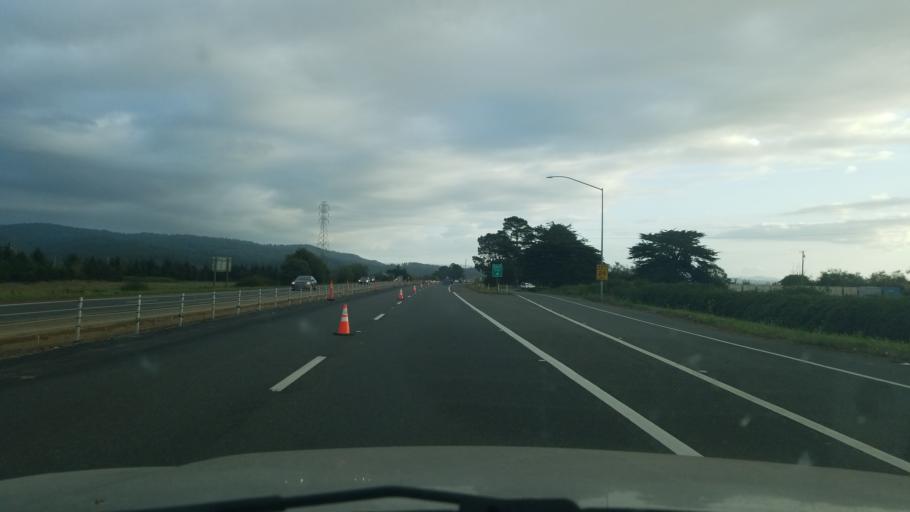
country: US
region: California
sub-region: Humboldt County
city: Arcata
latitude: 40.8534
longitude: -124.0822
